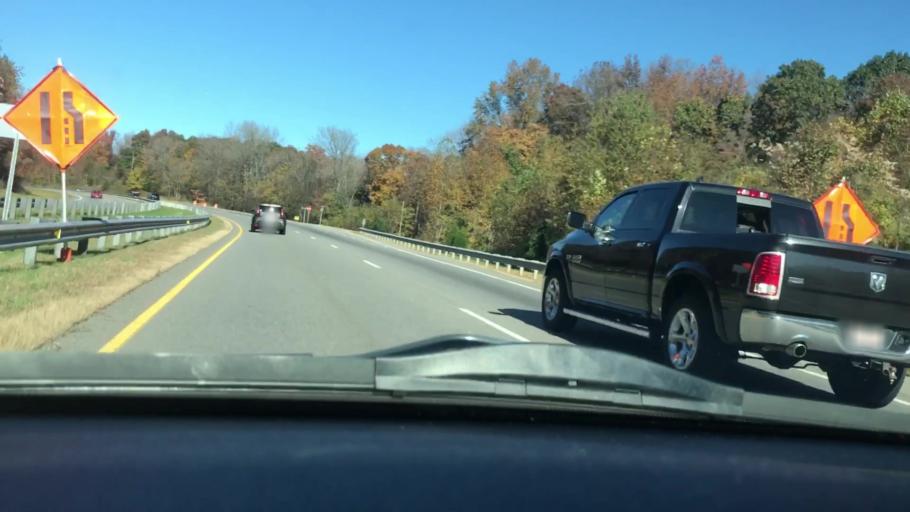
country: US
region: North Carolina
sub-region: Rockingham County
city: Mayodan
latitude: 36.4265
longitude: -79.9314
